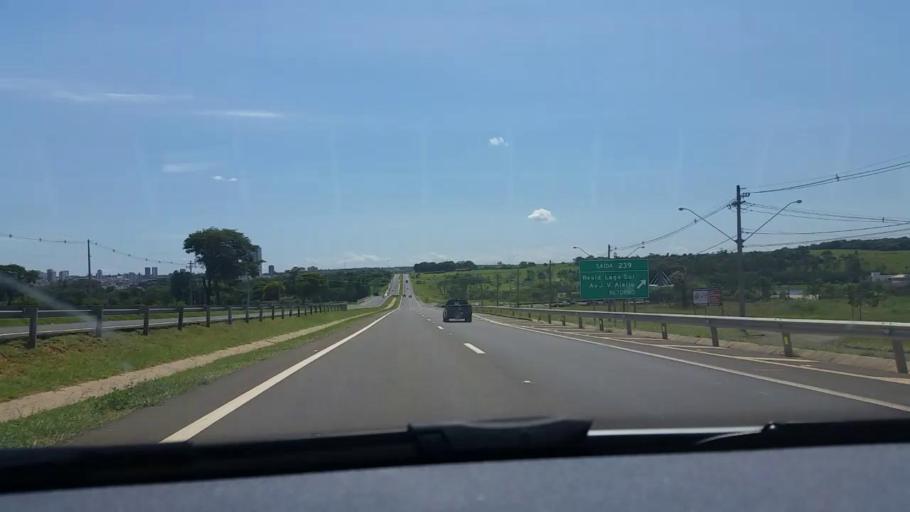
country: BR
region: Sao Paulo
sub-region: Bauru
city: Bauru
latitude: -22.3888
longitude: -49.0754
